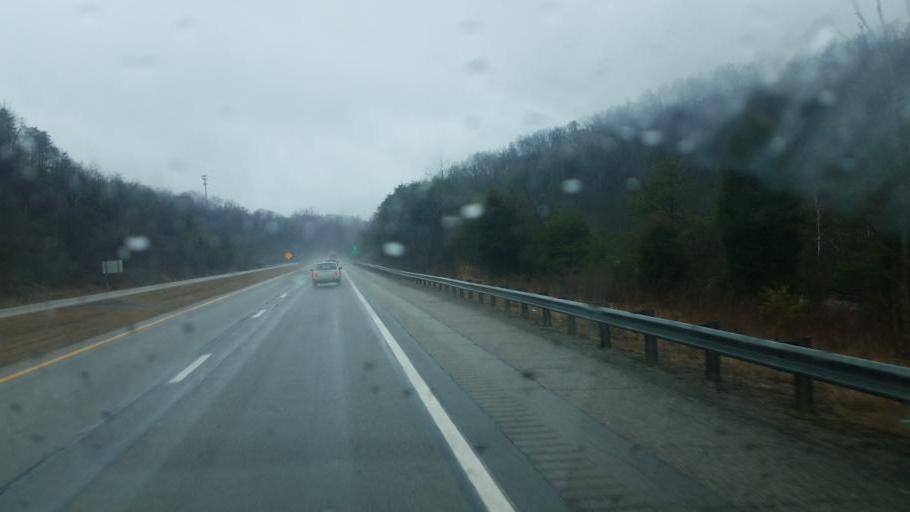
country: US
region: West Virginia
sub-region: Kanawha County
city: Sissonville
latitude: 38.4750
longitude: -81.6438
